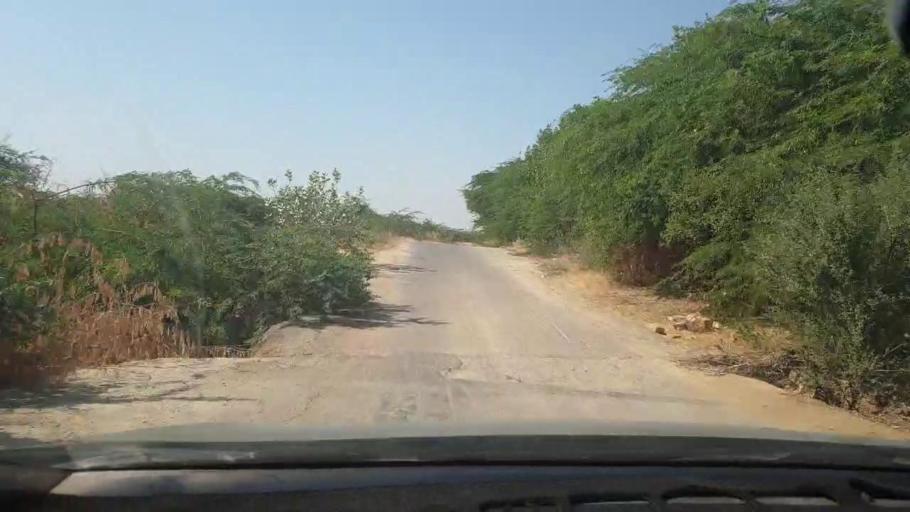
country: PK
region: Sindh
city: Malir Cantonment
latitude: 25.1618
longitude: 67.1566
